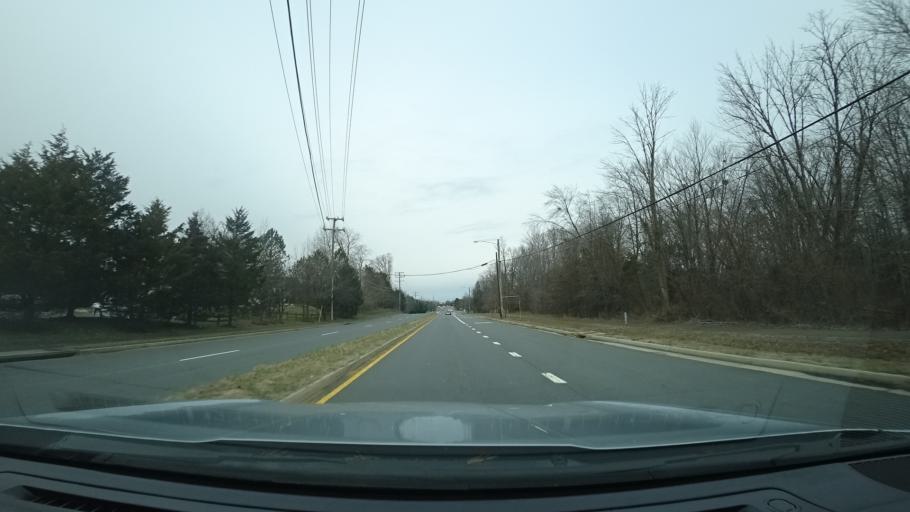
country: US
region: Virginia
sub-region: Fairfax County
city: Oak Hill
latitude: 38.9421
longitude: -77.3879
